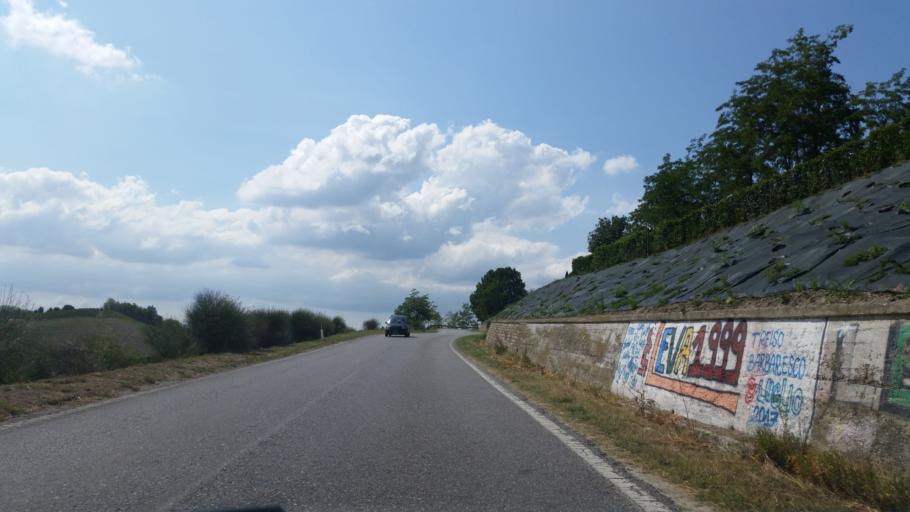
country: IT
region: Piedmont
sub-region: Provincia di Cuneo
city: Barbaresco
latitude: 44.7091
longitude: 8.0649
